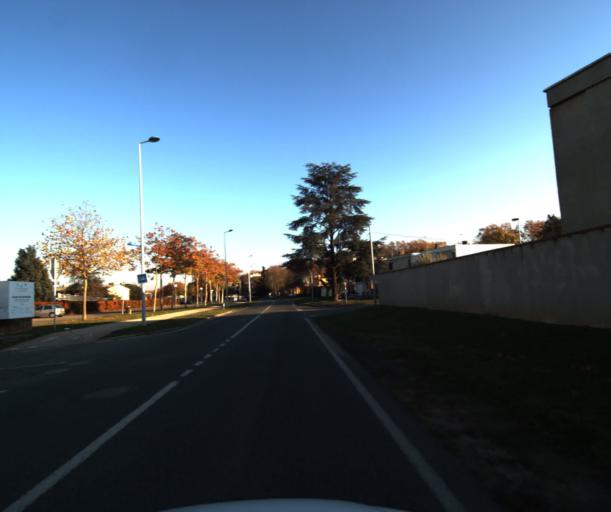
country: FR
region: Midi-Pyrenees
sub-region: Departement de la Haute-Garonne
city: Colomiers
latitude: 43.6104
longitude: 1.3477
